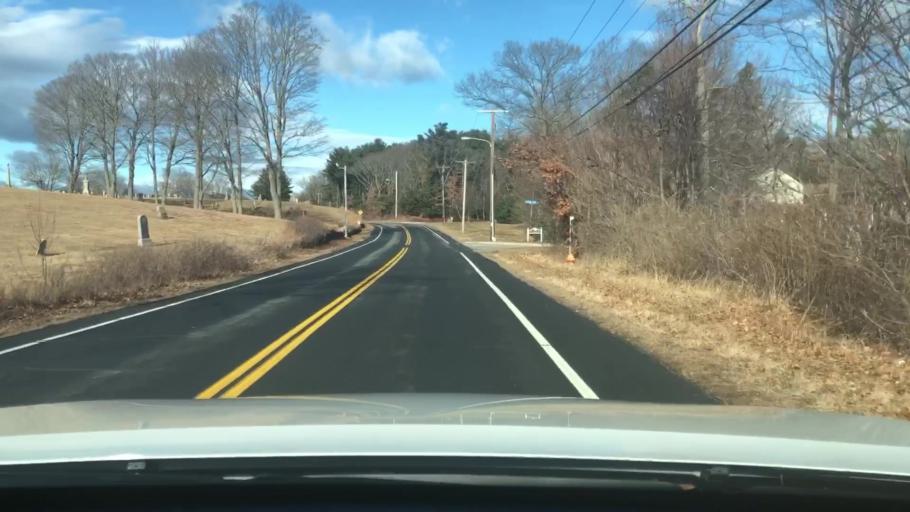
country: US
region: Rhode Island
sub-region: Providence County
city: Woonsocket
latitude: 42.0265
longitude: -71.5117
